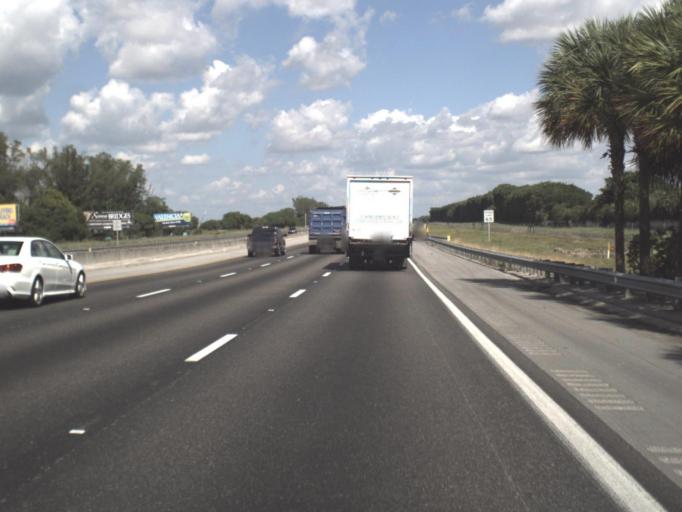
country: US
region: Florida
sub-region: Palm Beach County
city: Kings Point
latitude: 26.4128
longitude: -80.1713
